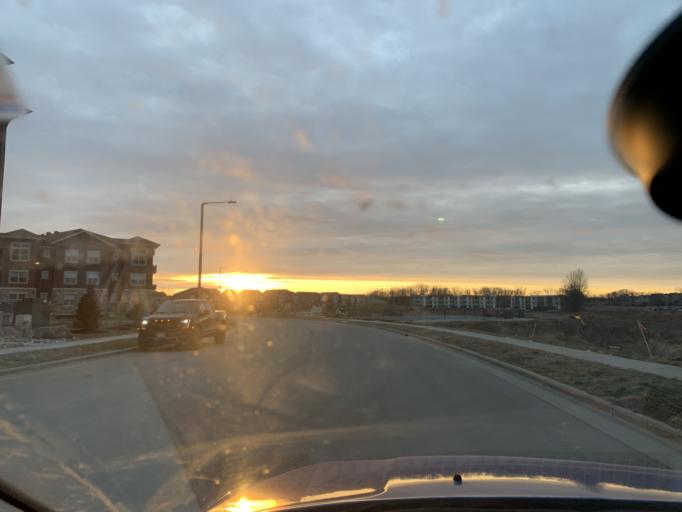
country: US
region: Wisconsin
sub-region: Dane County
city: Verona
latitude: 43.0530
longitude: -89.5534
